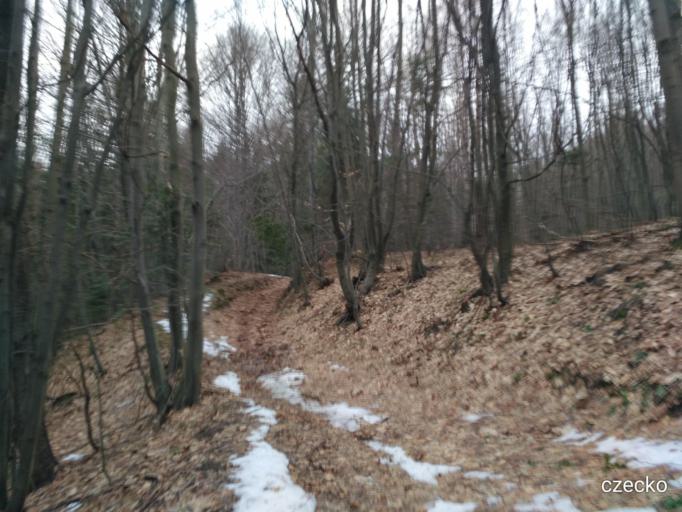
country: PL
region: Subcarpathian Voivodeship
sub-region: Powiat krosnienski
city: Korczyna
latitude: 49.7482
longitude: 21.8261
